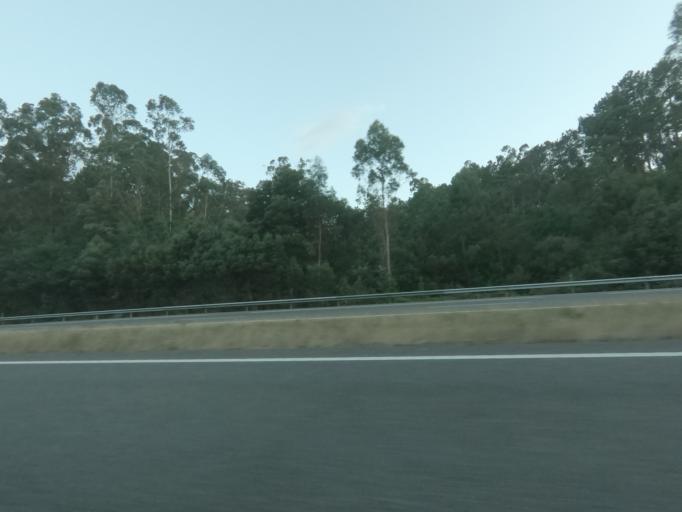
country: ES
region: Galicia
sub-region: Provincia de Pontevedra
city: Ponteareas
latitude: 42.1673
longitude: -8.5388
